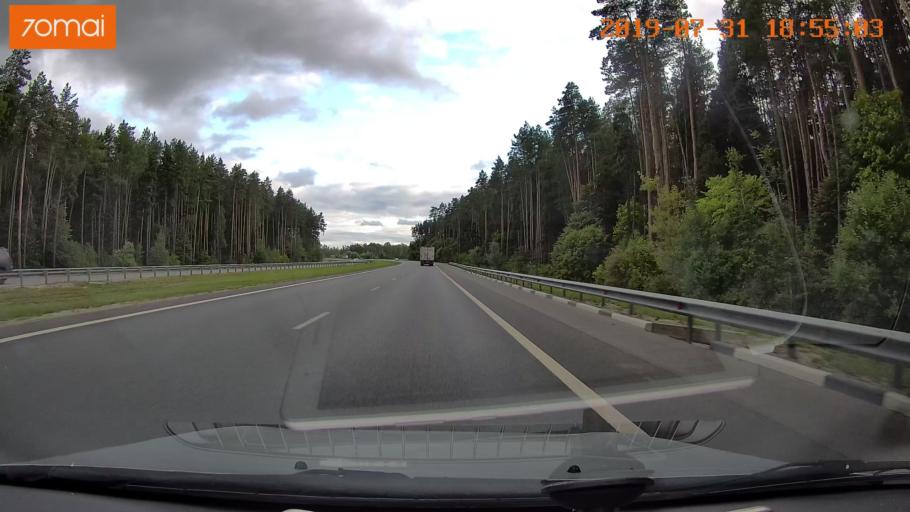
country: RU
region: Moskovskaya
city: Raduzhnyy
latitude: 55.1806
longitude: 38.6683
